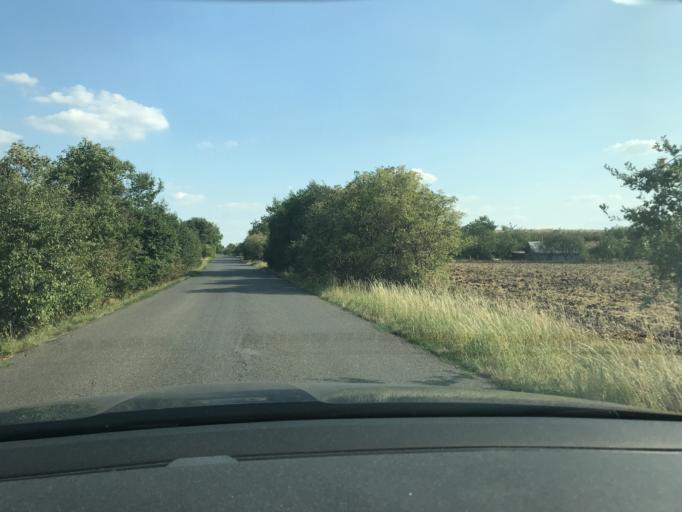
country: CZ
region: Central Bohemia
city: Kralupy nad Vltavou
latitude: 50.2305
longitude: 14.3167
